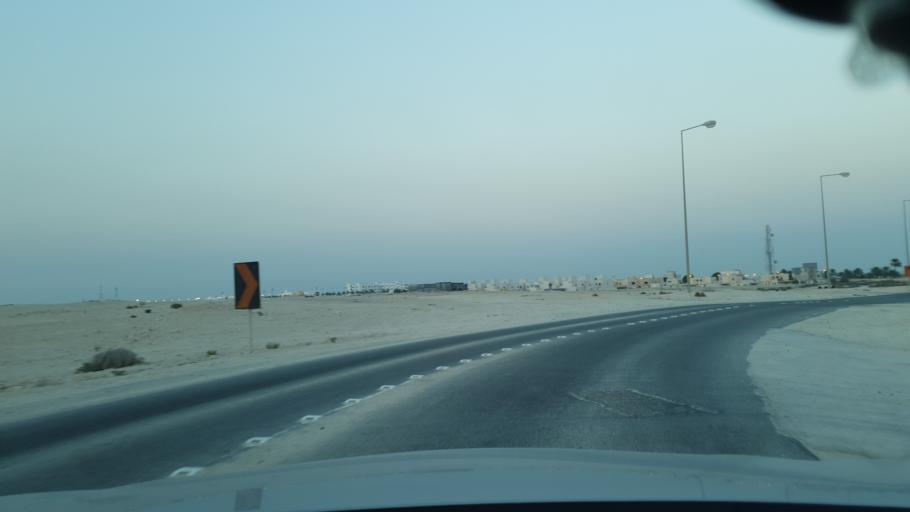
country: BH
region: Central Governorate
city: Dar Kulayb
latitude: 25.9766
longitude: 50.6100
